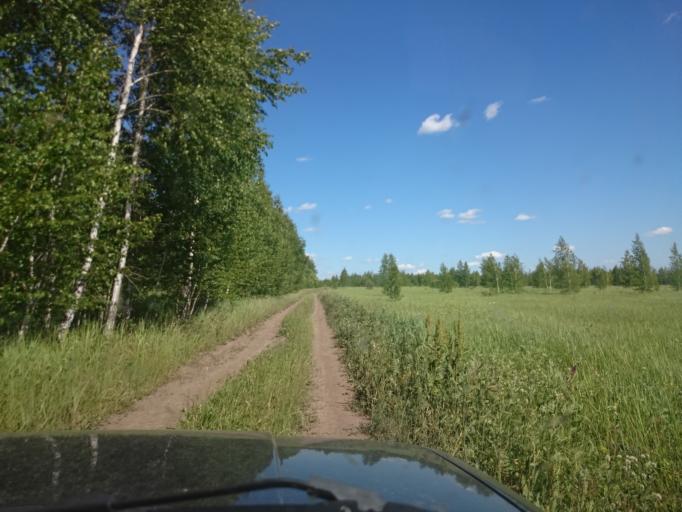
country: RU
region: Mordoviya
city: Kadoshkino
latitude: 54.0523
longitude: 44.4864
